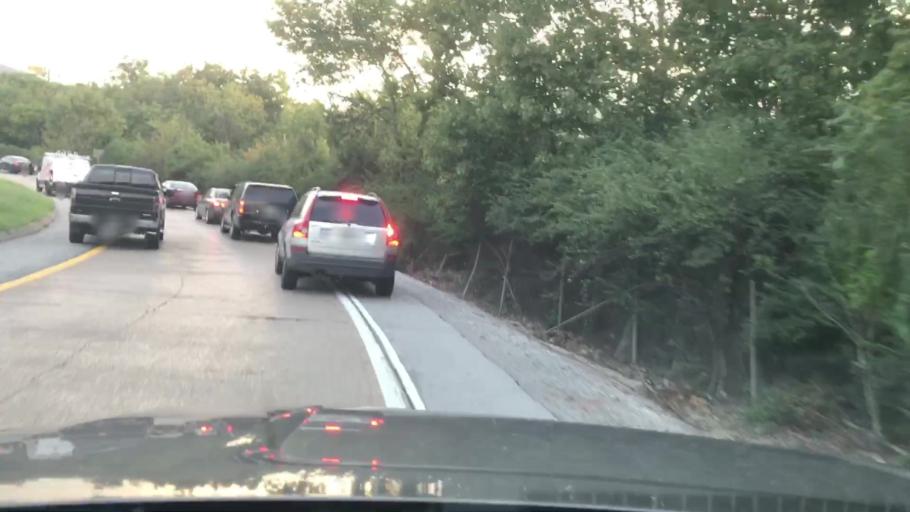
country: US
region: Tennessee
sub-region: Davidson County
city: Belle Meade
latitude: 36.1318
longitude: -86.9000
